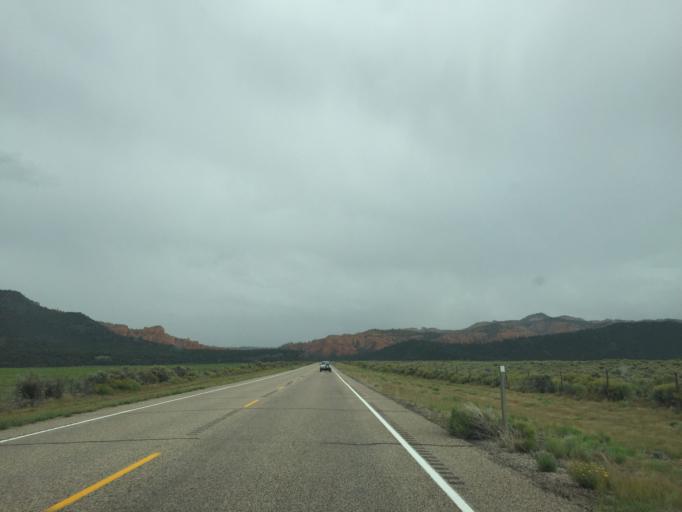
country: US
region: Utah
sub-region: Garfield County
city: Panguitch
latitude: 37.7475
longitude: -112.3545
